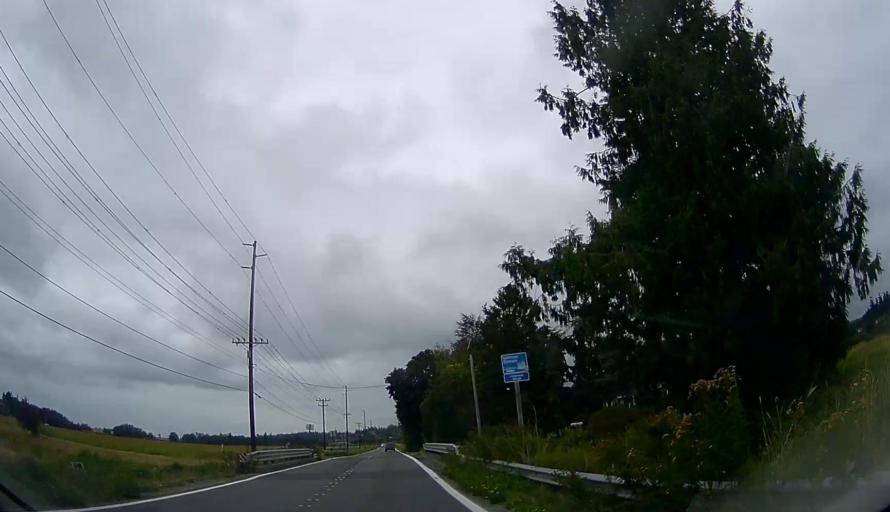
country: US
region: Washington
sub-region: Snohomish County
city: Stanwood
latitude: 48.2310
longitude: -122.3463
